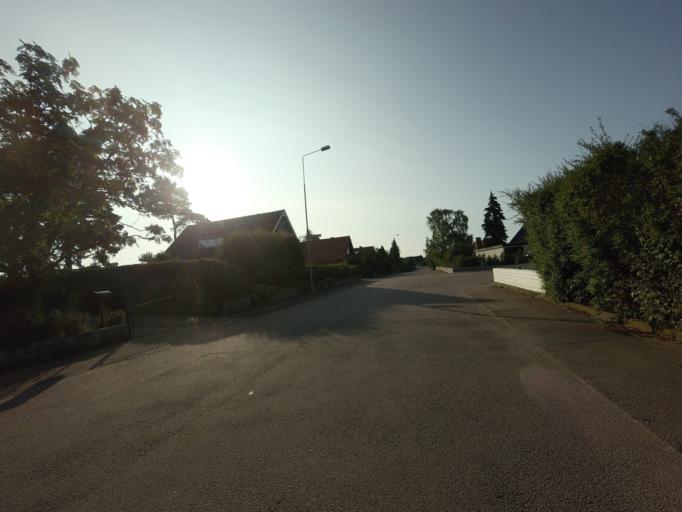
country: SE
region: Skane
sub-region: Landskrona
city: Asmundtorp
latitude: 55.8529
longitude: 12.9182
